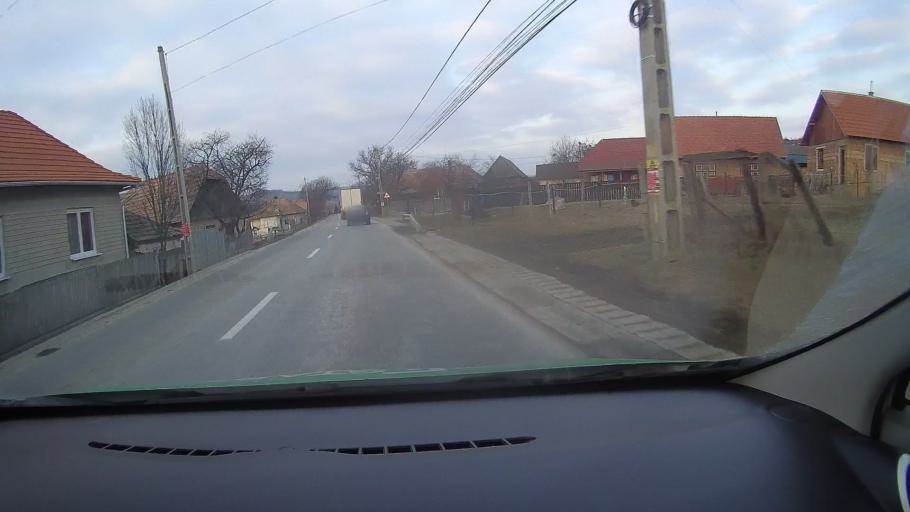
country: RO
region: Harghita
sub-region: Comuna Simonesti
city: Simonesti
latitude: 46.3416
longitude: 25.1142
